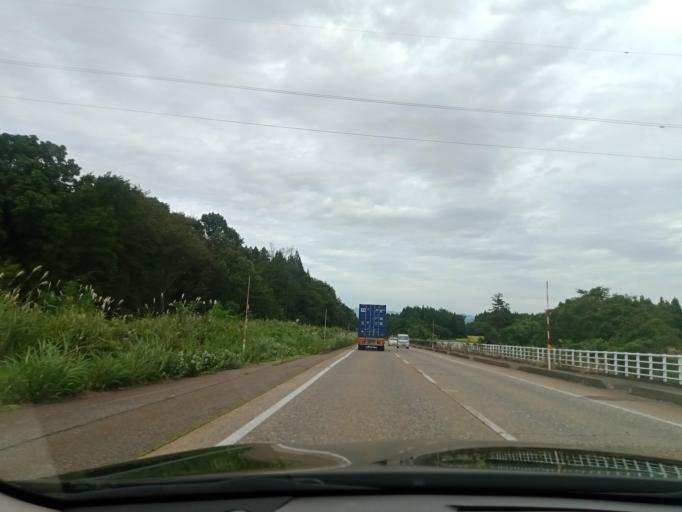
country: JP
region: Niigata
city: Arai
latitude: 36.9989
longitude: 138.2214
